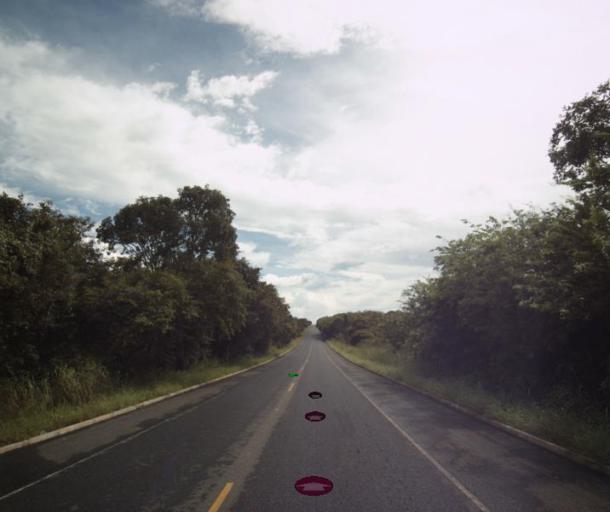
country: BR
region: Goias
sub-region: Sao Miguel Do Araguaia
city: Sao Miguel do Araguaia
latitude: -13.2872
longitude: -50.1954
